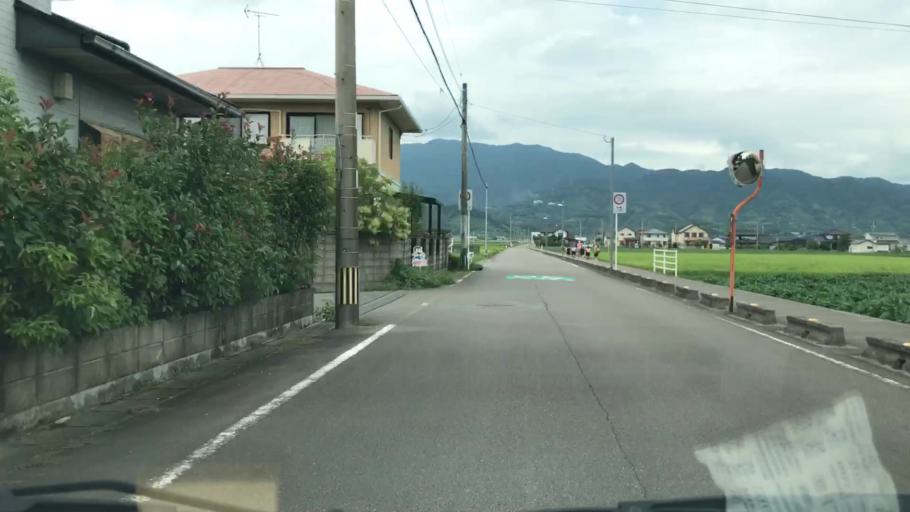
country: JP
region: Saga Prefecture
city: Saga-shi
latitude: 33.2827
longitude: 130.2261
